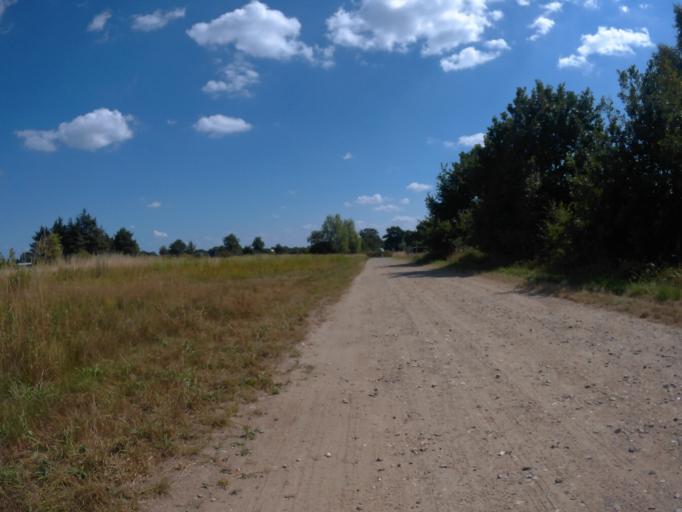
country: DE
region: Schleswig-Holstein
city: Suderstapel
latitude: 54.3603
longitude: 9.2227
